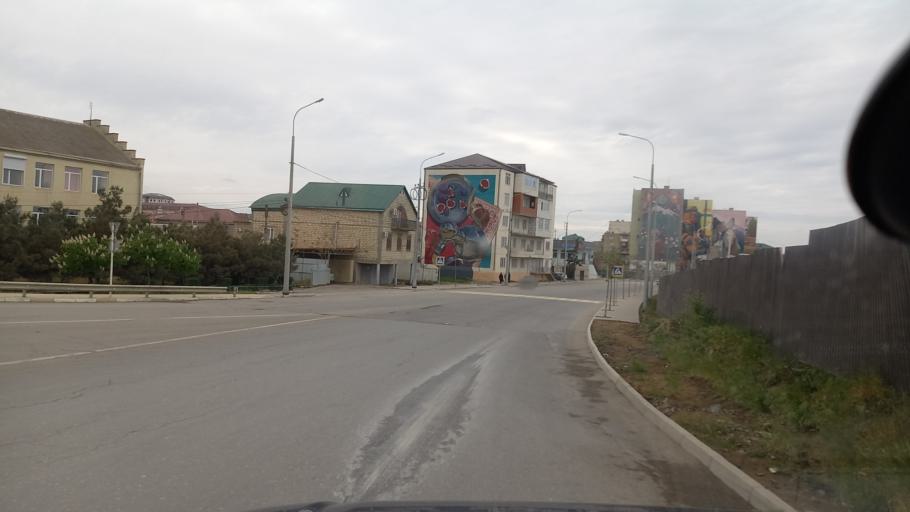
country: RU
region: Dagestan
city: Derbent
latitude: 42.0726
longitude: 48.3003
